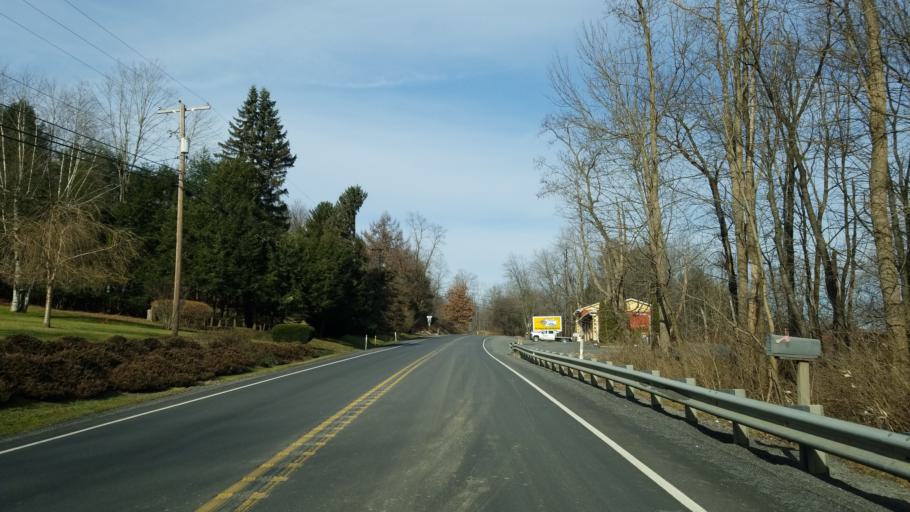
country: US
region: Pennsylvania
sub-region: Clearfield County
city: Curwensville
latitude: 40.9593
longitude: -78.6120
